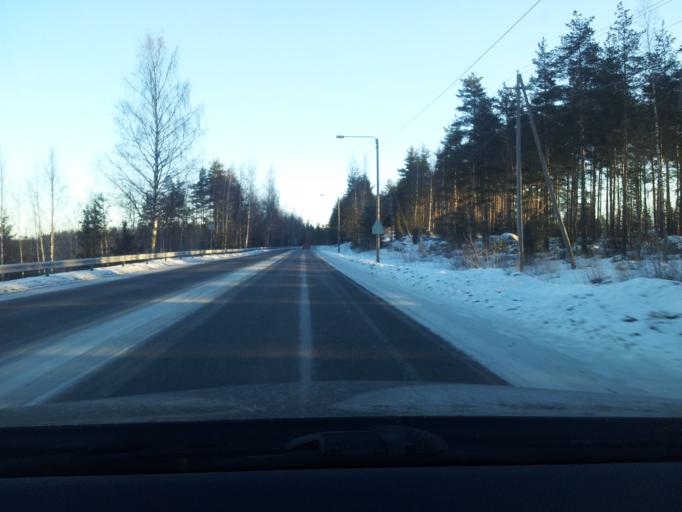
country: FI
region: Uusimaa
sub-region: Helsinki
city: Vihti
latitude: 60.3540
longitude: 24.3342
